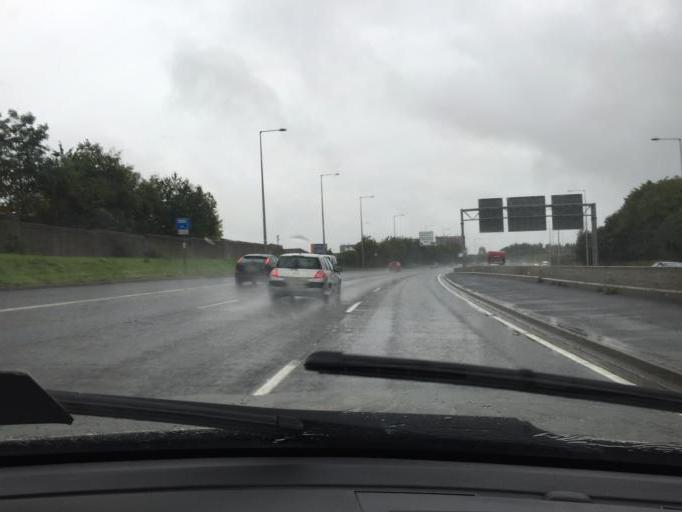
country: IE
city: Palmerstown
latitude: 53.3557
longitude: -6.3941
